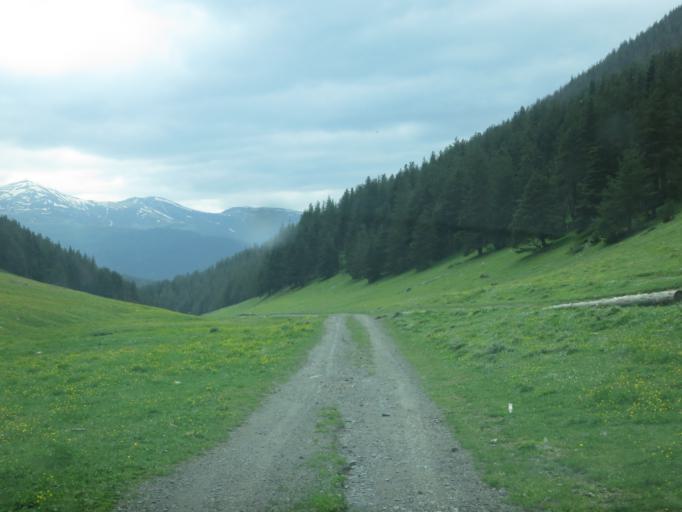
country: RU
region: Chechnya
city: Itum-Kali
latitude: 42.3882
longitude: 45.6751
